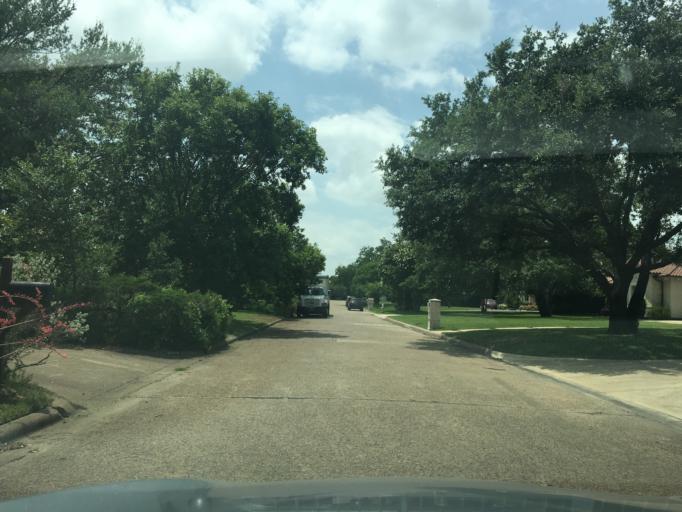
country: US
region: Texas
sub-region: Dallas County
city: University Park
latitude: 32.8932
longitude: -96.8299
